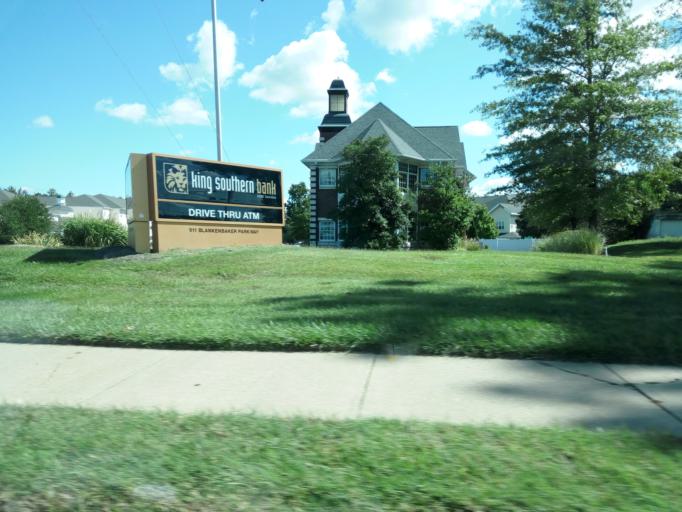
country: US
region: Kentucky
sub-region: Jefferson County
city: Douglass Hills
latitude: 38.2276
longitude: -85.5409
